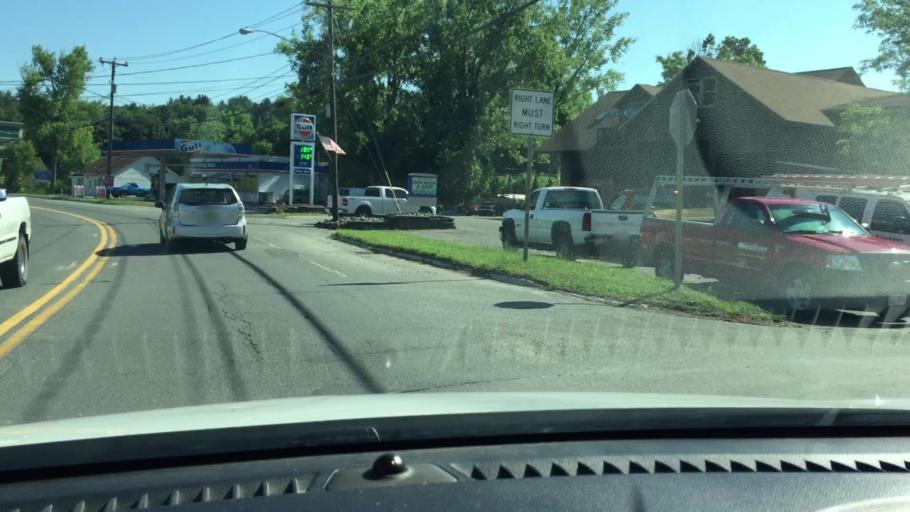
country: US
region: Massachusetts
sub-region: Berkshire County
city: Lanesborough
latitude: 42.4948
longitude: -73.2378
